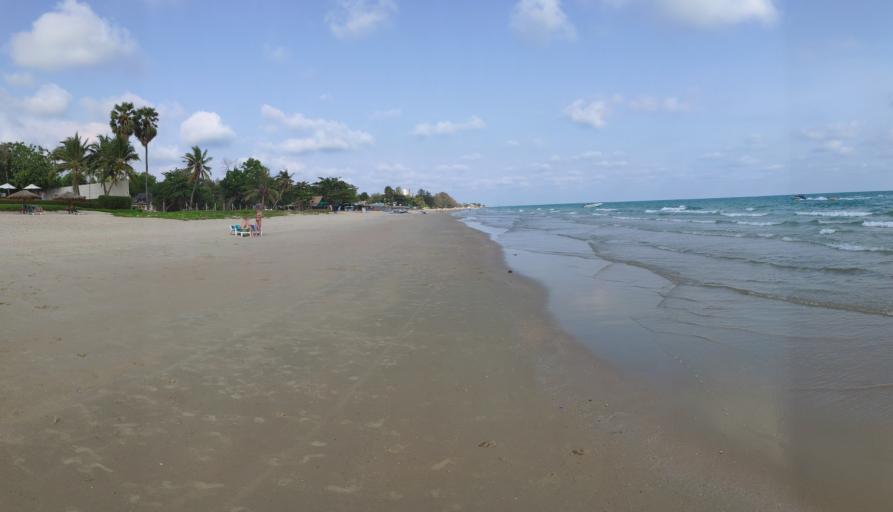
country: TH
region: Rayong
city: Klaeng
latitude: 12.6294
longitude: 101.5420
